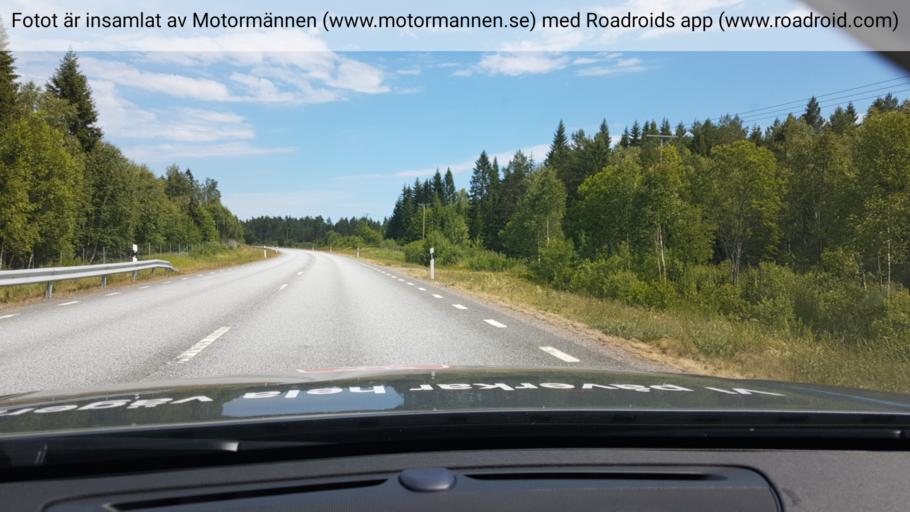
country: SE
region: Uppsala
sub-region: Osthammars Kommun
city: Anneberg
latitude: 60.1714
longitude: 18.3797
